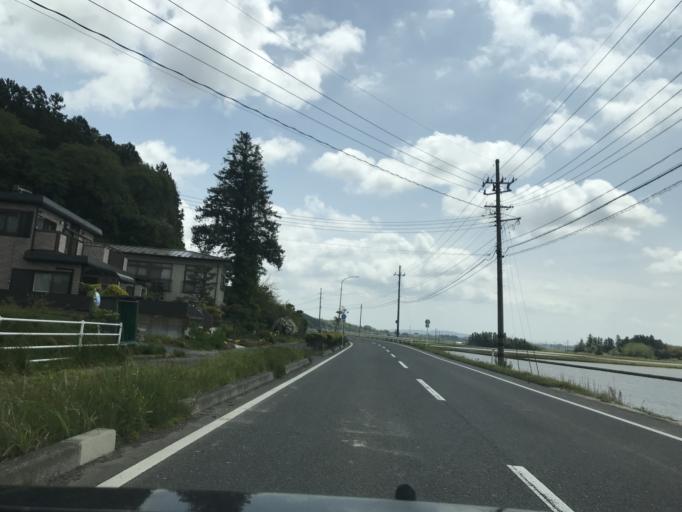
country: JP
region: Miyagi
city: Furukawa
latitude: 38.6725
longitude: 140.9873
